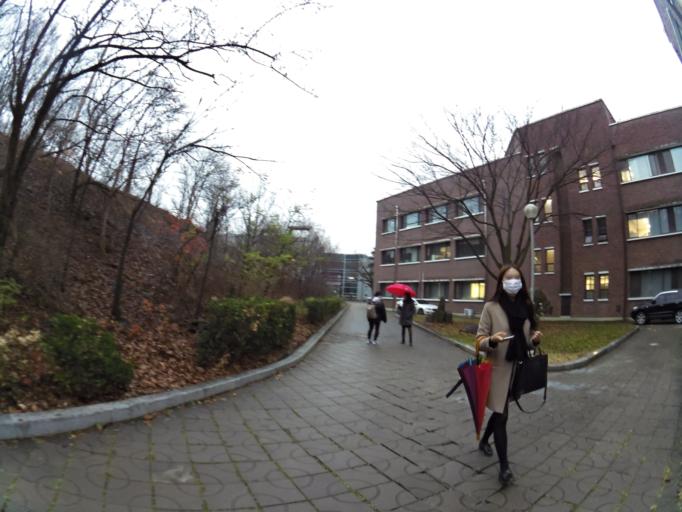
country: KR
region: Gyeongsangbuk-do
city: Gyeongsan-si
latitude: 35.8353
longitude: 128.7575
